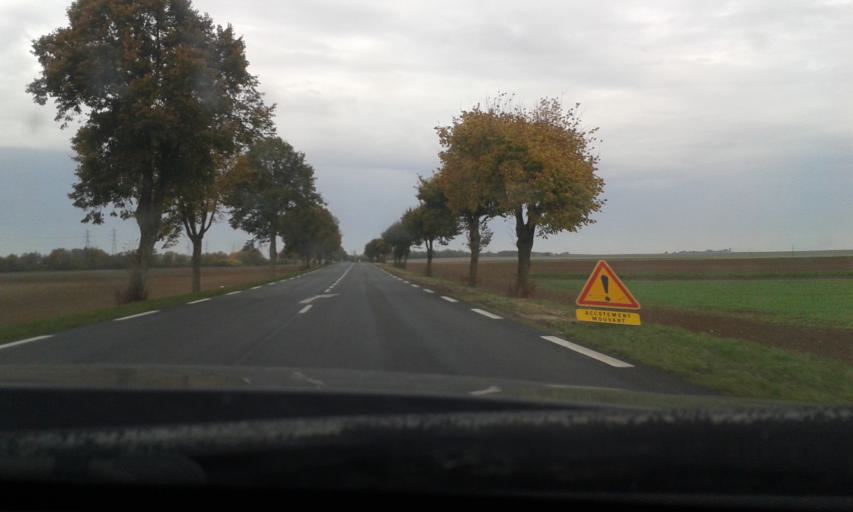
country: FR
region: Centre
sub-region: Departement d'Eure-et-Loir
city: Baigneaux
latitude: 48.1232
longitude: 1.8569
